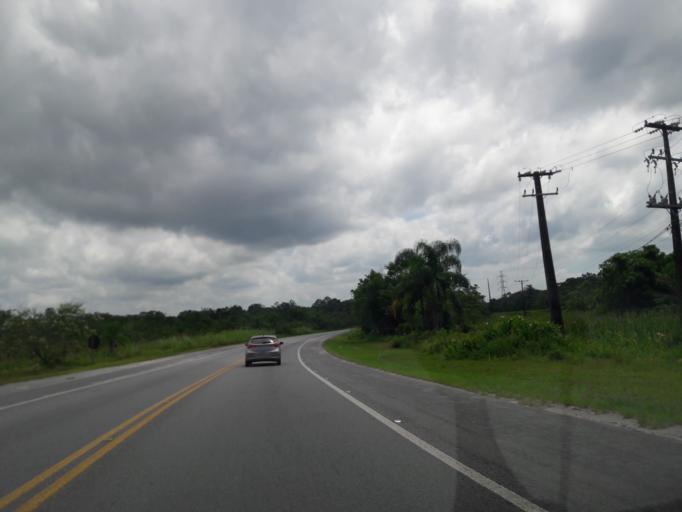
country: BR
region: Parana
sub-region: Pontal Do Parana
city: Pontal do Parana
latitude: -25.6709
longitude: -48.5146
